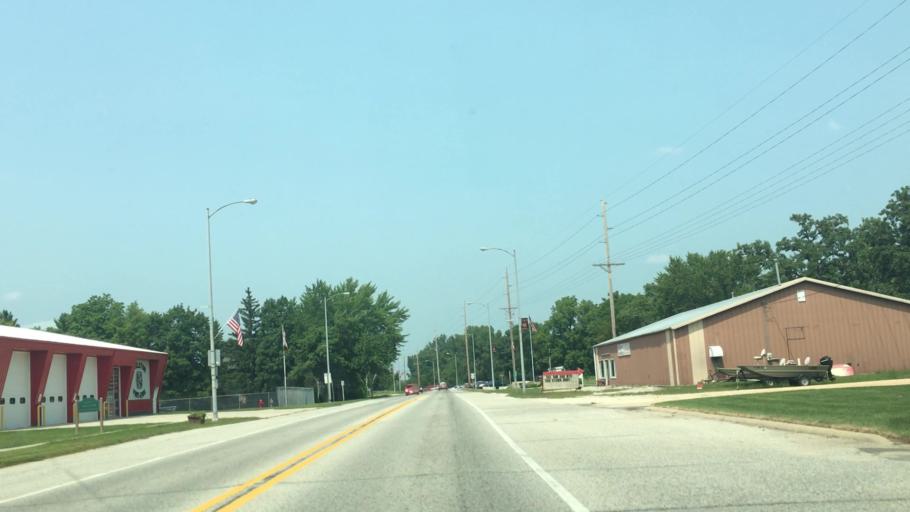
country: US
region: Iowa
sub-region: Fayette County
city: Oelwein
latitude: 42.6183
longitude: -91.9056
